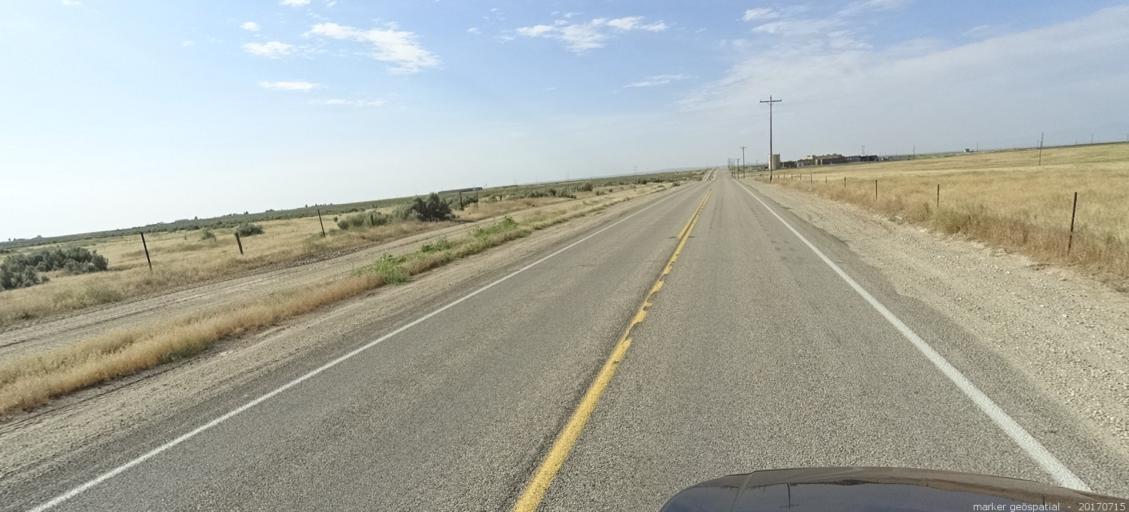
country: US
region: Idaho
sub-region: Ada County
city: Boise
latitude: 43.4671
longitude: -116.2343
